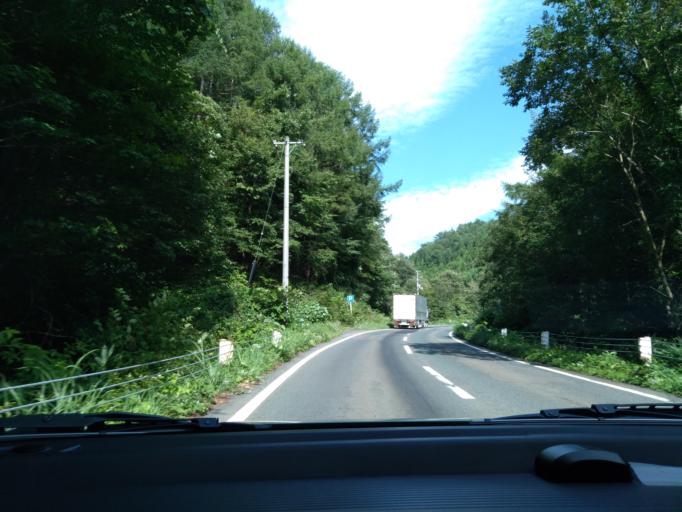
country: JP
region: Iwate
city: Shizukuishi
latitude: 39.6400
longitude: 141.0132
